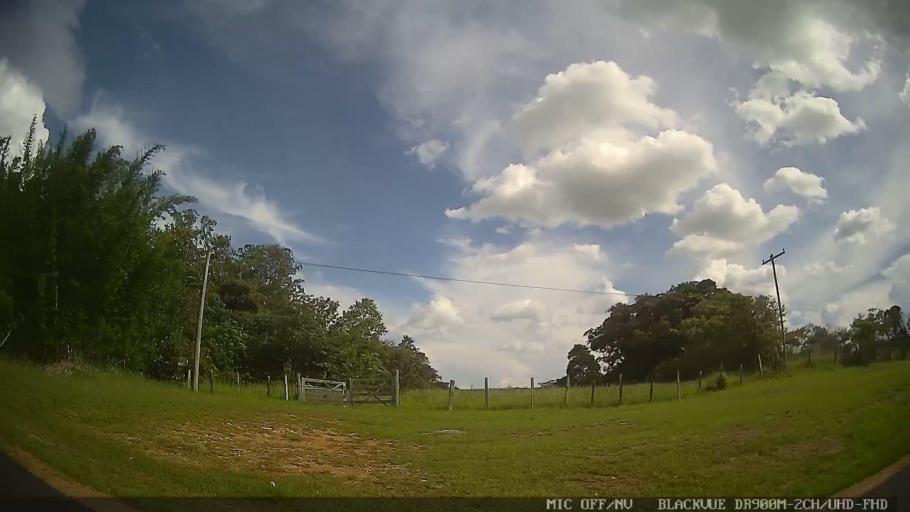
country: BR
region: Sao Paulo
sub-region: Laranjal Paulista
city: Laranjal Paulista
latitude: -23.0452
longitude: -47.9163
